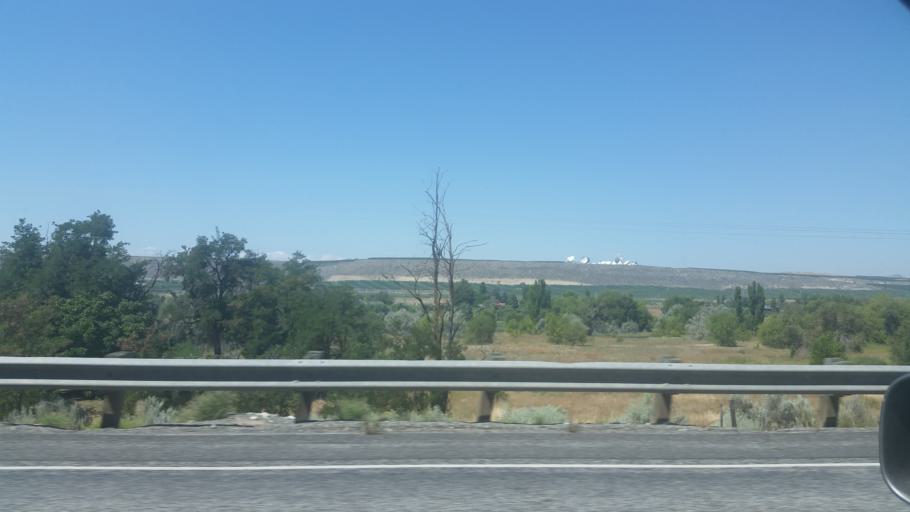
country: US
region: Washington
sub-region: Okanogan County
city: Brewster
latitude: 48.1357
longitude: -119.6699
